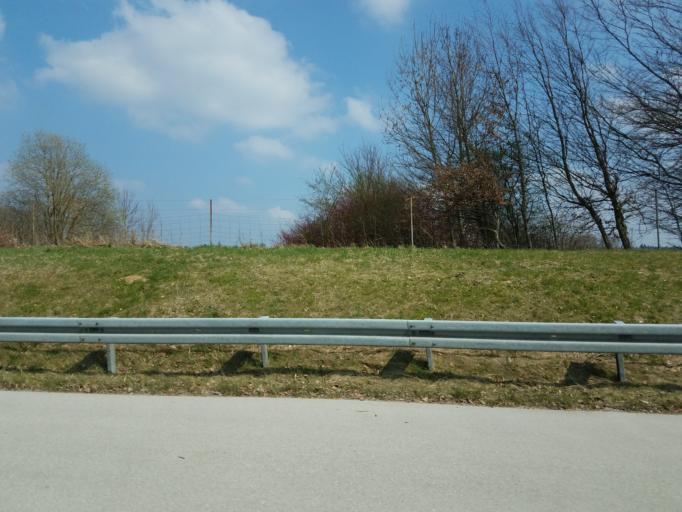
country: DE
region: Bavaria
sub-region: Upper Bavaria
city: Schaftlarn
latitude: 48.0190
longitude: 11.4203
